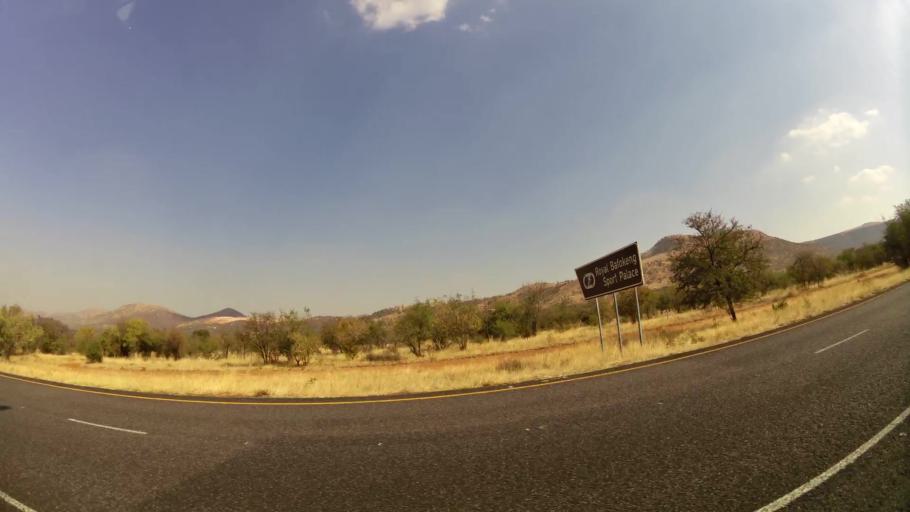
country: ZA
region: North-West
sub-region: Bojanala Platinum District Municipality
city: Rustenburg
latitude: -25.6064
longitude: 27.1425
